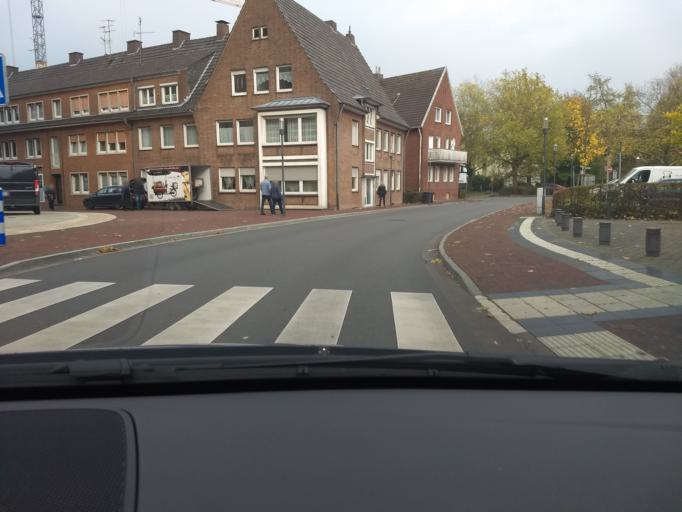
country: DE
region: North Rhine-Westphalia
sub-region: Regierungsbezirk Munster
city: Borken
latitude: 51.8439
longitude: 6.8604
